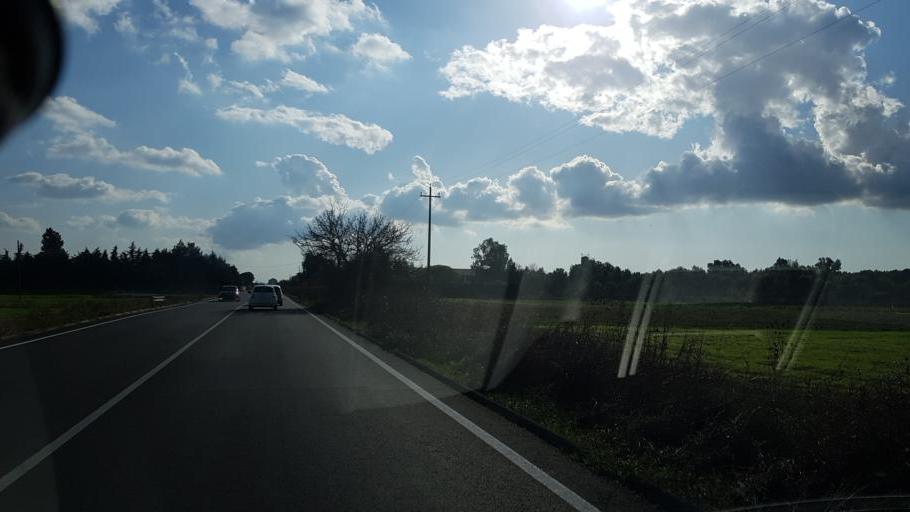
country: IT
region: Apulia
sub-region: Provincia di Lecce
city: Salice Salentino
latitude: 40.3703
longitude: 17.9669
